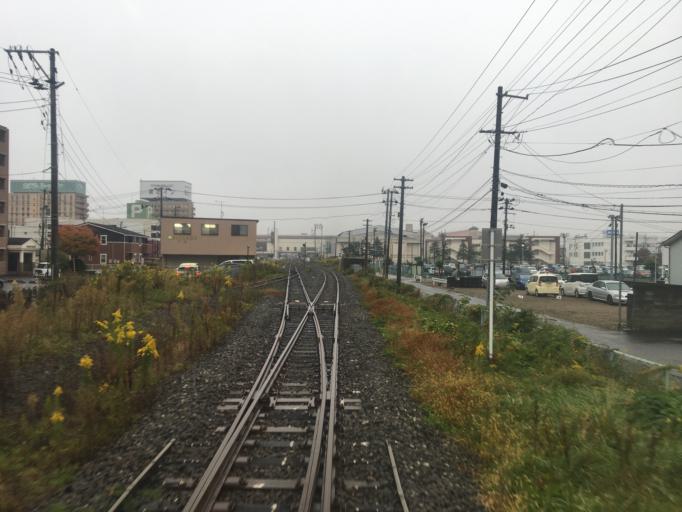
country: JP
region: Miyagi
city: Furukawa
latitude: 38.5710
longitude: 140.9621
